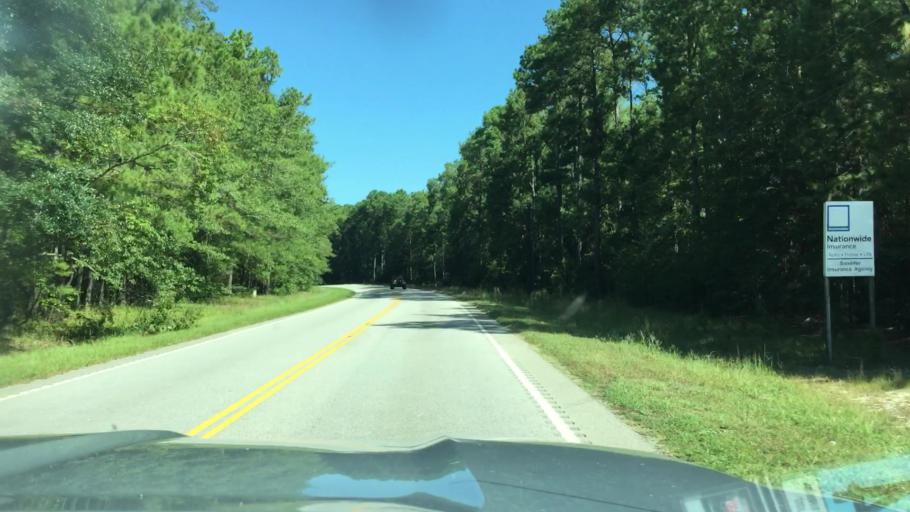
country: US
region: South Carolina
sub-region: Chesterfield County
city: Cheraw
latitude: 34.6387
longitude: -79.8861
